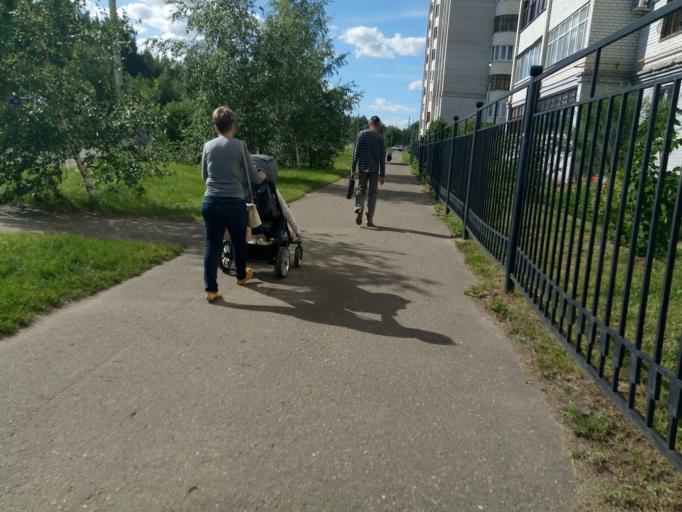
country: RU
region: Jaroslavl
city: Yaroslavl
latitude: 57.6401
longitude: 39.9475
